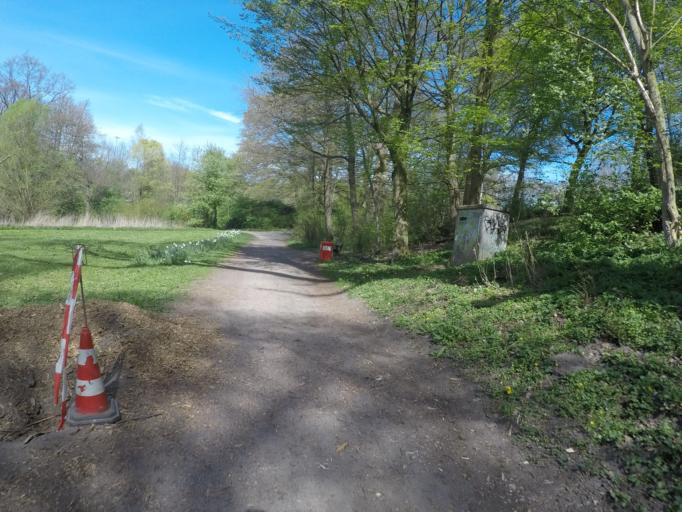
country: DE
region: Hamburg
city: Poppenbuettel
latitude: 53.6553
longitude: 10.0874
